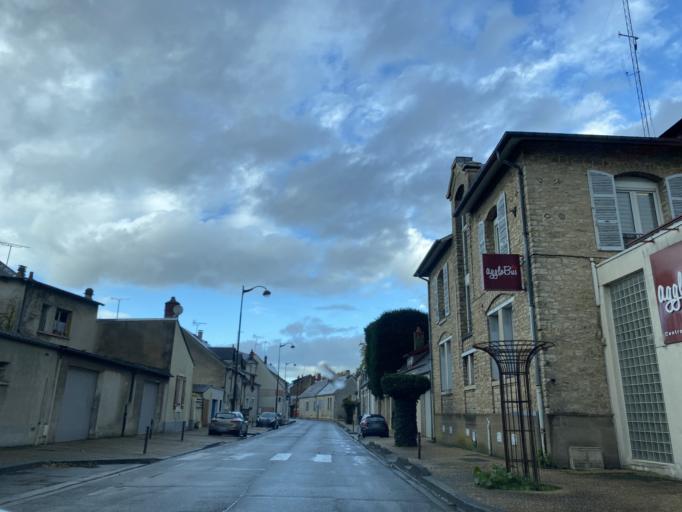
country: FR
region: Centre
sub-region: Departement du Cher
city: Bourges
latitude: 47.0759
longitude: 2.3903
